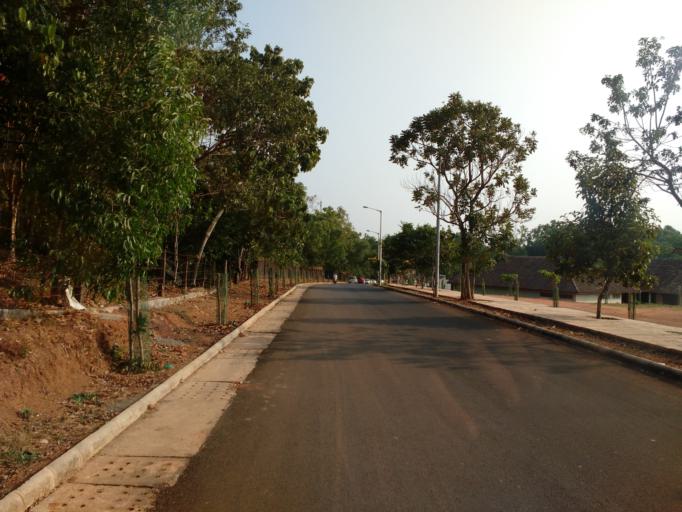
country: IN
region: Karnataka
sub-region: Dakshina Kannada
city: Mangalore
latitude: 12.9295
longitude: 74.8991
